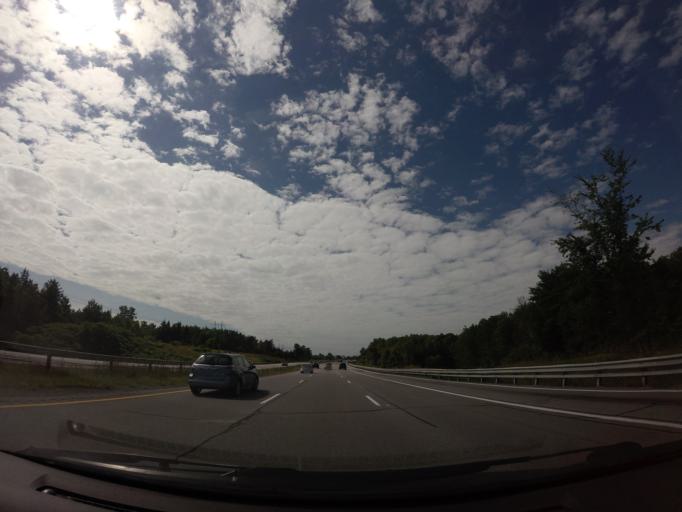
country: CA
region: Ontario
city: Ottawa
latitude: 45.4433
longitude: -75.5891
